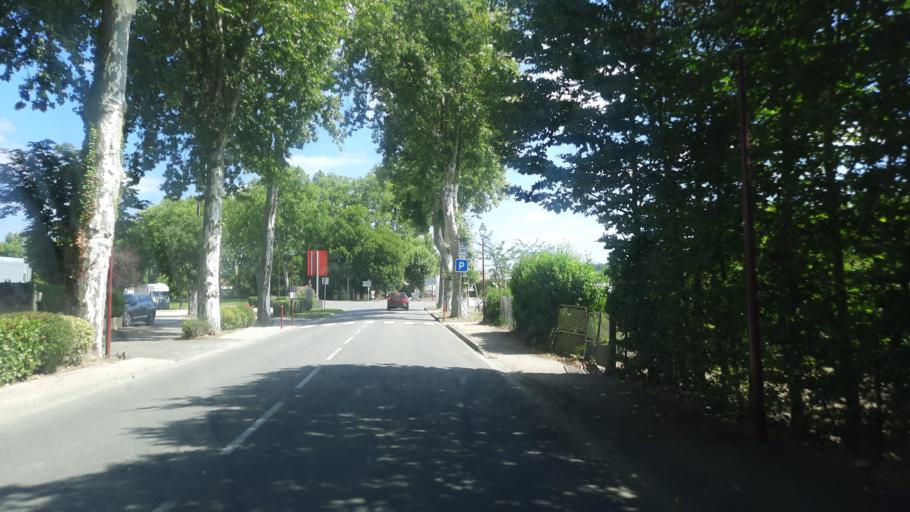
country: FR
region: Midi-Pyrenees
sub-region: Departement du Gers
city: Lombez
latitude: 43.4745
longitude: 0.9153
